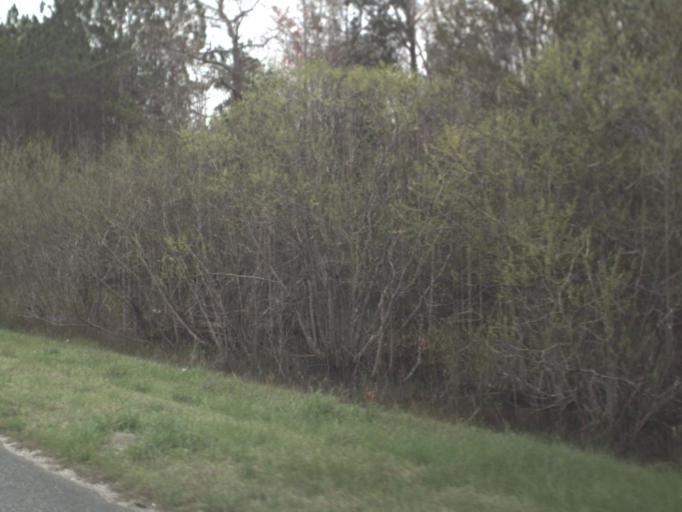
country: US
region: Florida
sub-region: Leon County
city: Woodville
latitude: 30.1949
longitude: -84.1370
